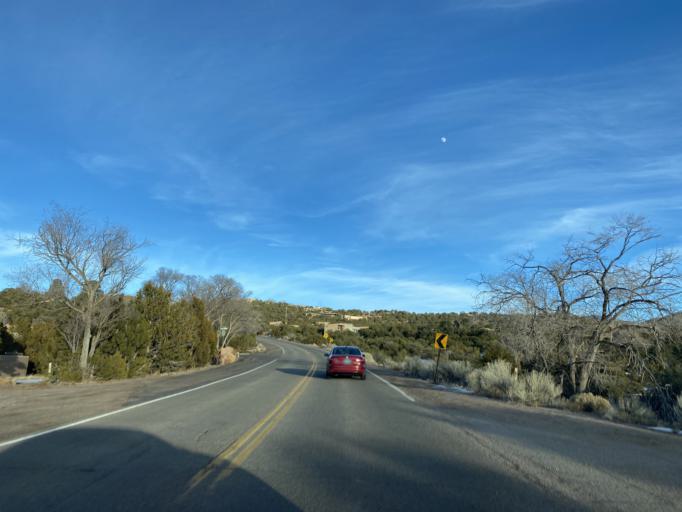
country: US
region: New Mexico
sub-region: Santa Fe County
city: Santa Fe
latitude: 35.6949
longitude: -105.9149
